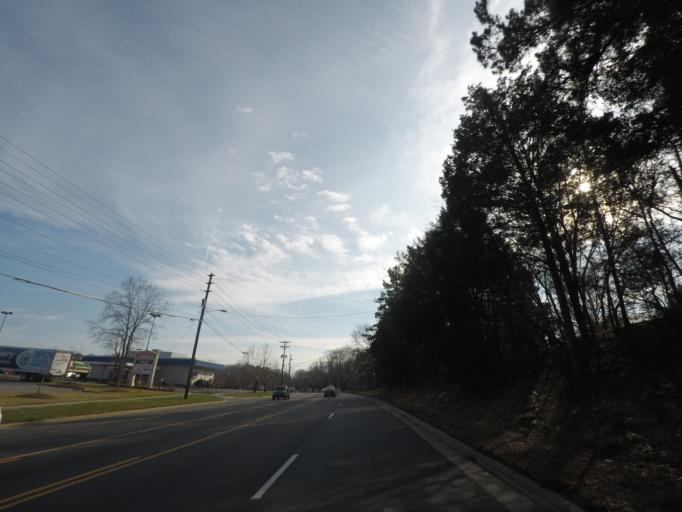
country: US
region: North Carolina
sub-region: Durham County
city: Durham
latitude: 36.0691
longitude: -78.9079
